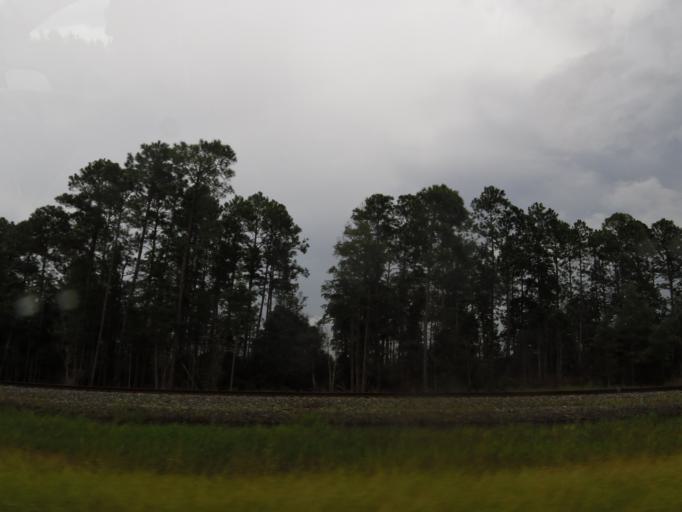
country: US
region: Georgia
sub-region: Wayne County
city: Jesup
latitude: 31.4908
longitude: -81.7439
